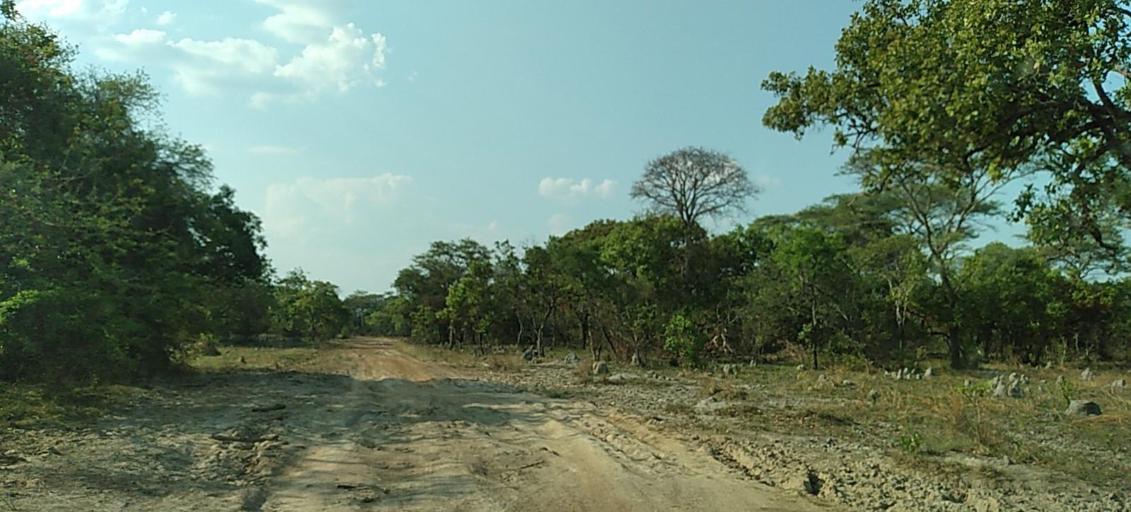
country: ZM
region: Copperbelt
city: Mpongwe
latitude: -13.4411
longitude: 28.0613
